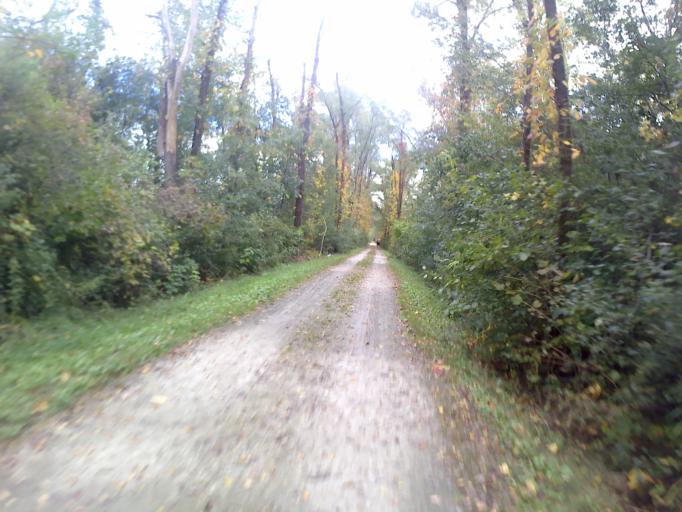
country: US
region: Illinois
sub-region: DuPage County
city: Wayne
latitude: 41.9583
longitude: -88.2496
